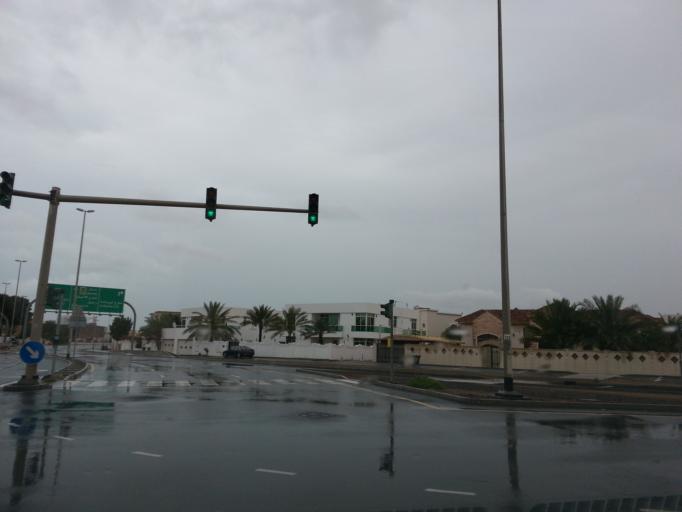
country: AE
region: Dubai
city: Dubai
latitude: 25.0940
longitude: 55.2040
